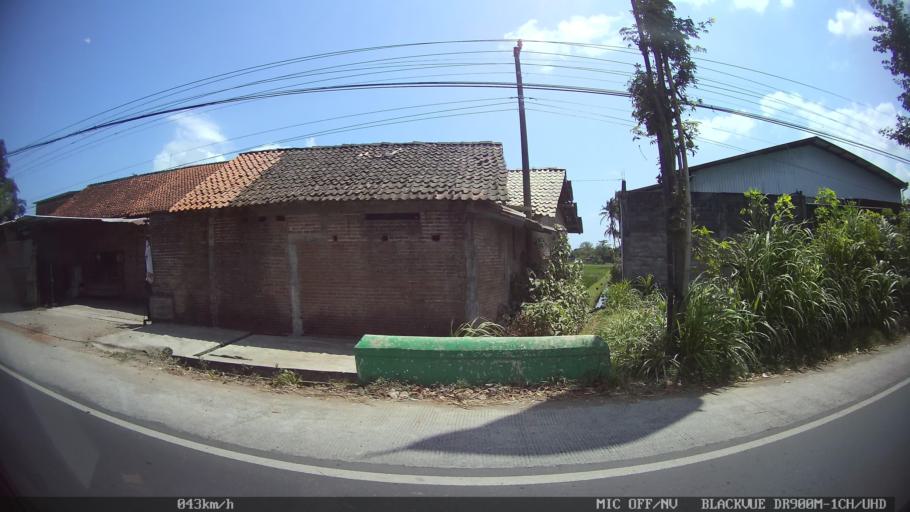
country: ID
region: Daerah Istimewa Yogyakarta
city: Pundong
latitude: -7.9343
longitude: 110.3738
